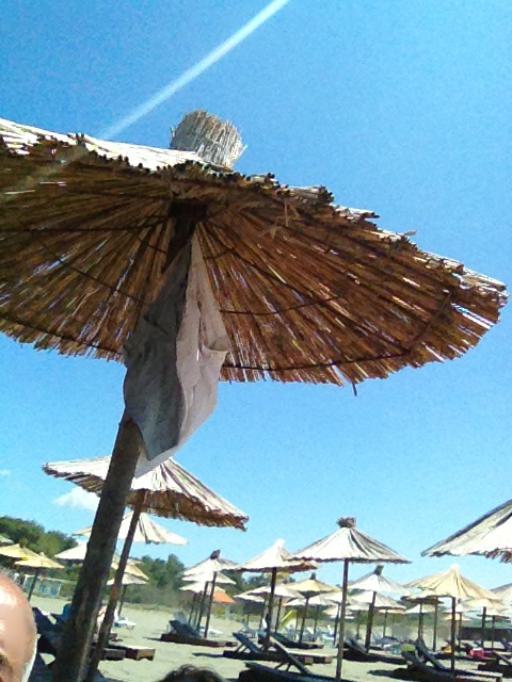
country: ME
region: Ulcinj
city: Ulcinj
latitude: 41.9093
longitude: 19.2407
